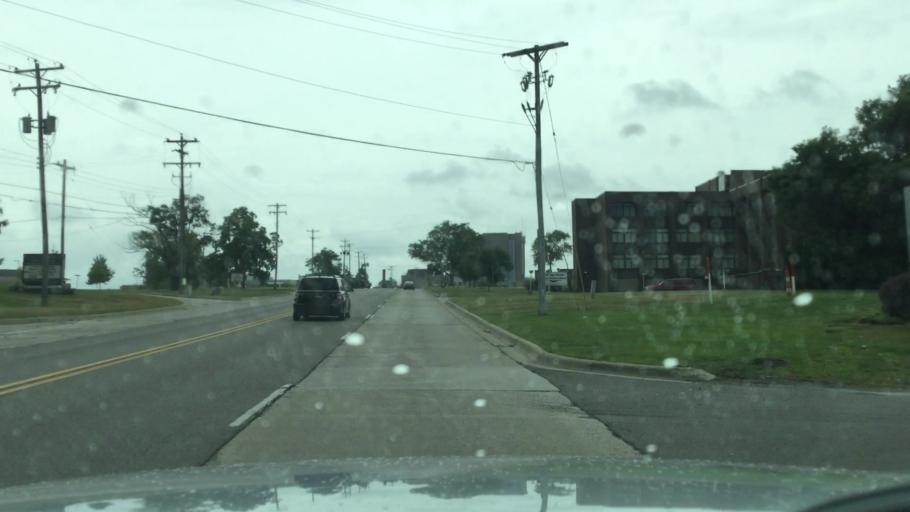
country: US
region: Michigan
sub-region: Genesee County
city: Flint
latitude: 43.0154
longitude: -83.7403
